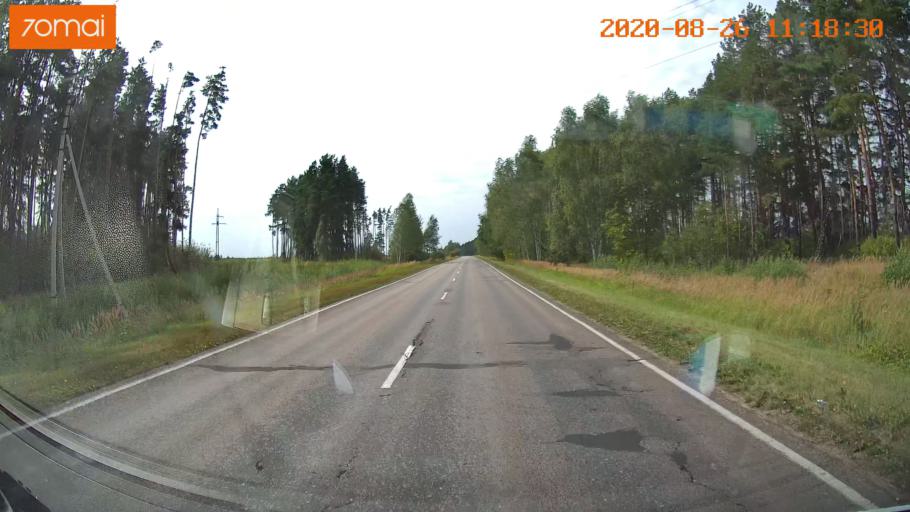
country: RU
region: Rjazan
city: Shilovo
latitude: 54.4095
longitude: 41.0964
